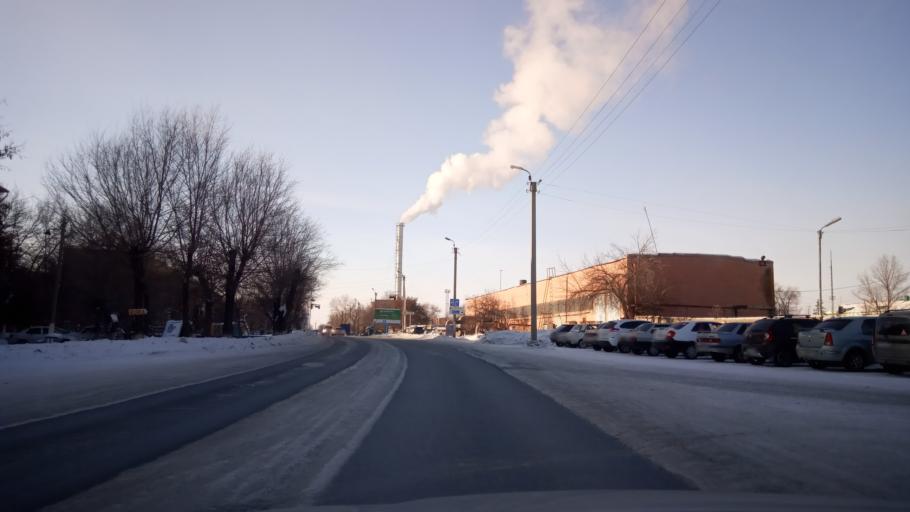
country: RU
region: Orenburg
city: Novotroitsk
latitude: 51.2002
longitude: 58.3126
